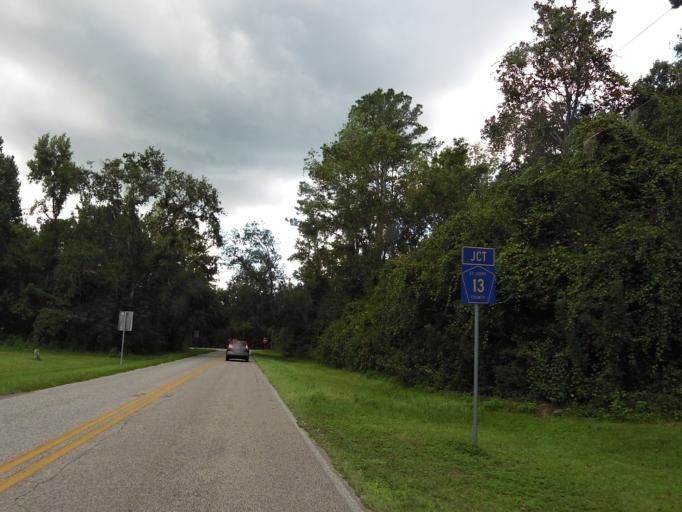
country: US
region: Florida
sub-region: Putnam County
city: East Palatka
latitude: 29.7788
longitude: -81.4857
